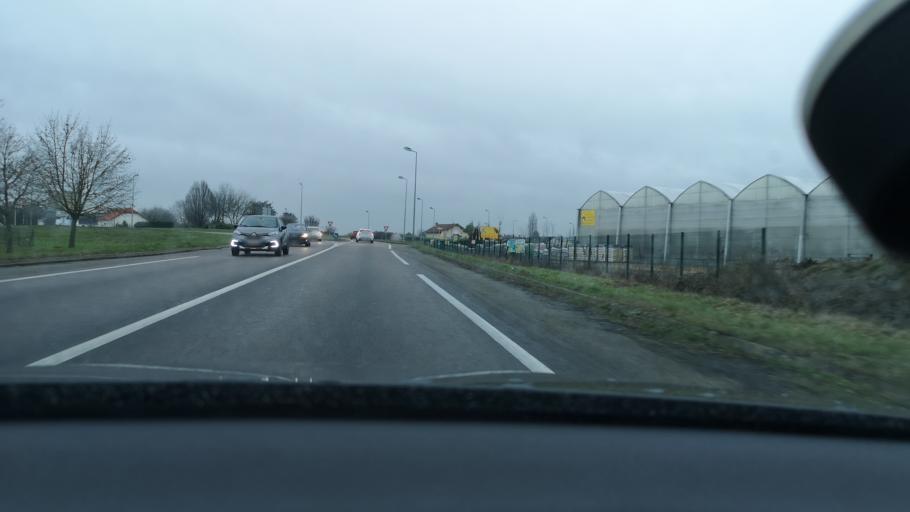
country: FR
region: Bourgogne
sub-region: Departement de Saone-et-Loire
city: Saint-Marcel
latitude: 46.7860
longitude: 4.9079
